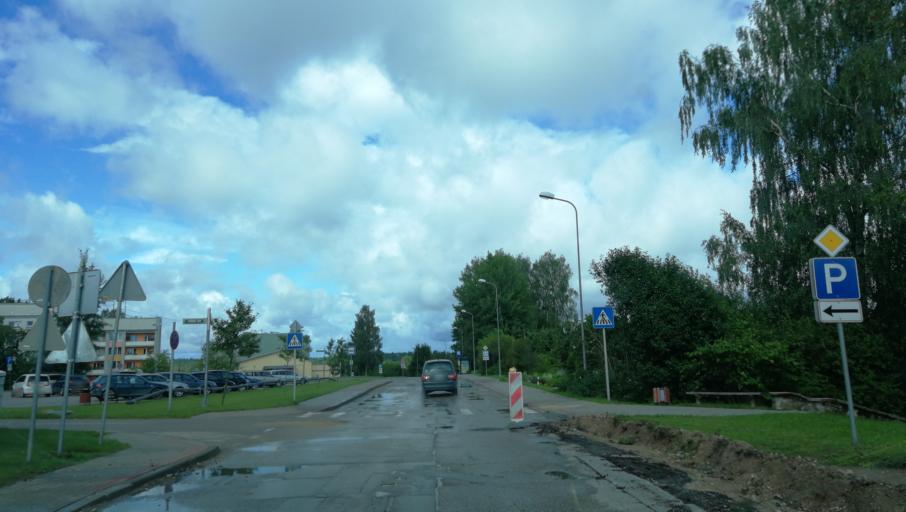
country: LV
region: Cesu Rajons
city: Cesis
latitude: 57.3147
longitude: 25.2587
